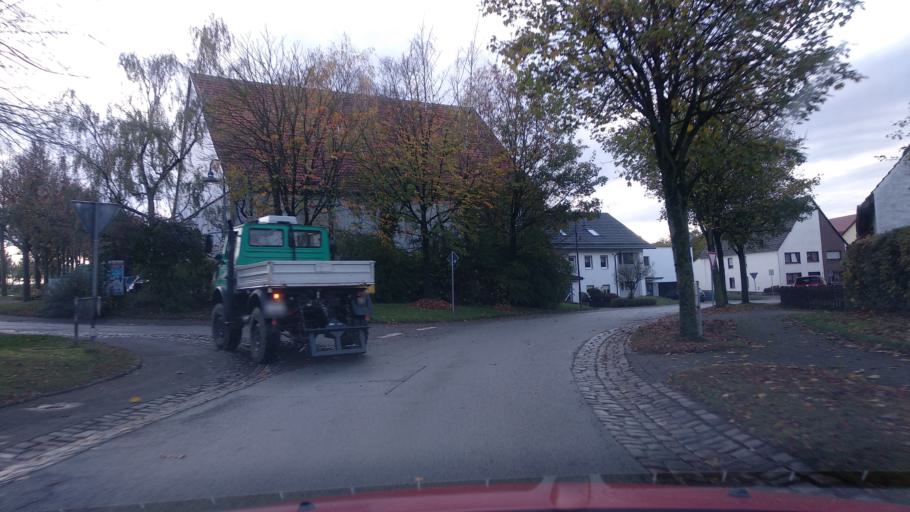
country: DE
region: North Rhine-Westphalia
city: Borgentreich
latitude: 51.6577
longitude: 9.2756
